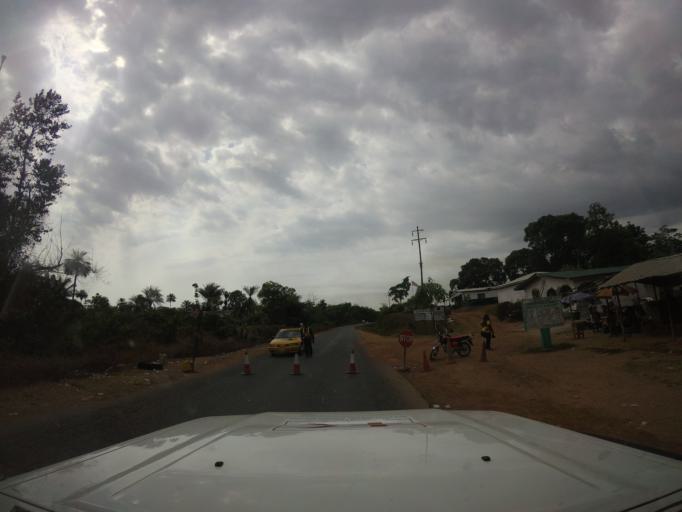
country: LR
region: Montserrado
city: Monrovia
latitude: 6.5362
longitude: -10.8534
